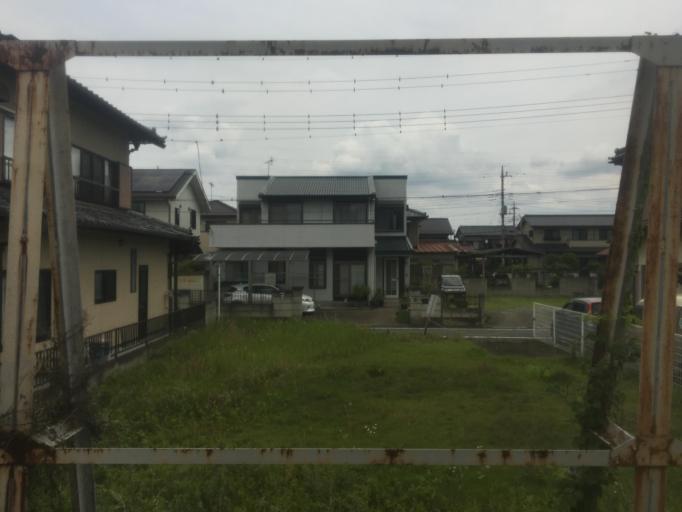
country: JP
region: Gunma
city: Yoshii
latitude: 36.2559
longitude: 138.9659
